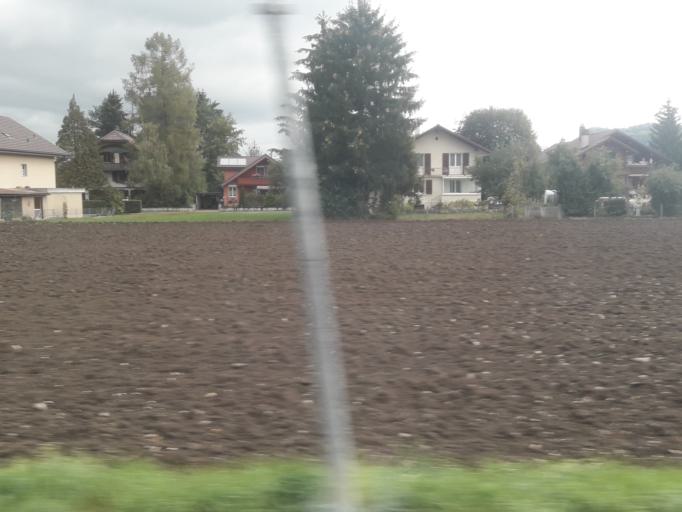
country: CH
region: Bern
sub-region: Thun District
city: Uetendorf
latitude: 46.7732
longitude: 7.5940
